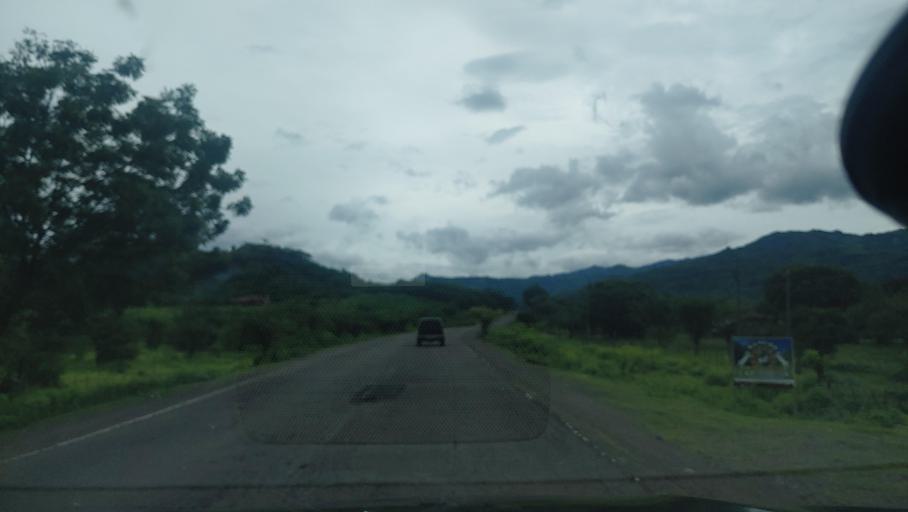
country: HN
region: Choluteca
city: Santa Ana de Yusguare
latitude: 13.3564
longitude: -87.1006
